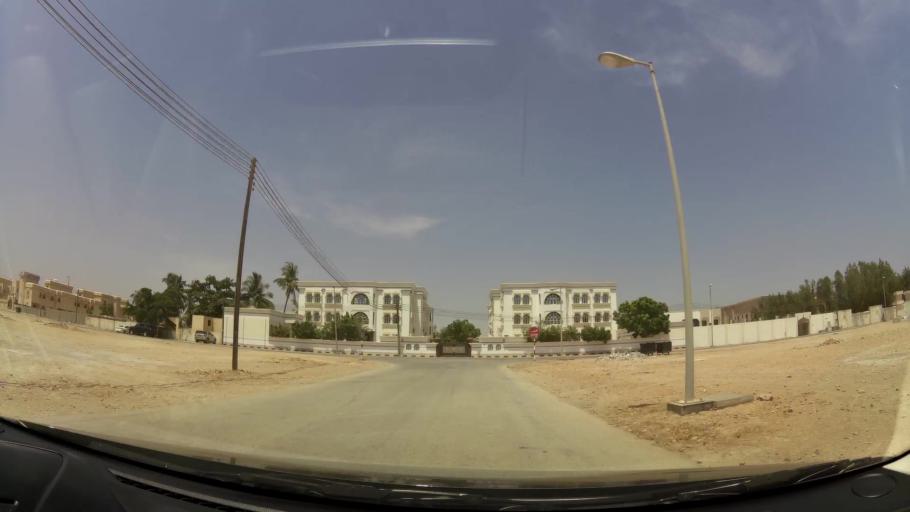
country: OM
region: Zufar
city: Salalah
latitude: 17.0566
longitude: 54.1542
